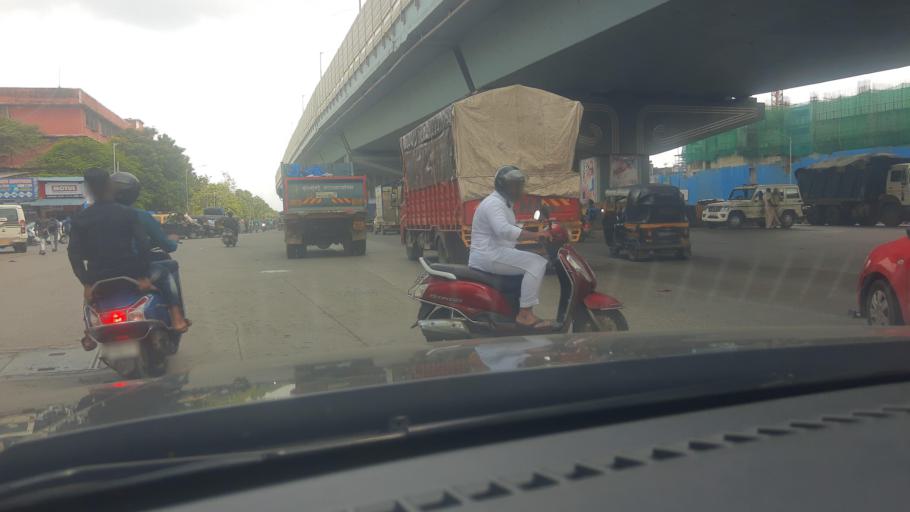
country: IN
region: Maharashtra
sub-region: Mumbai Suburban
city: Mumbai
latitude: 19.0605
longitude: 72.9186
